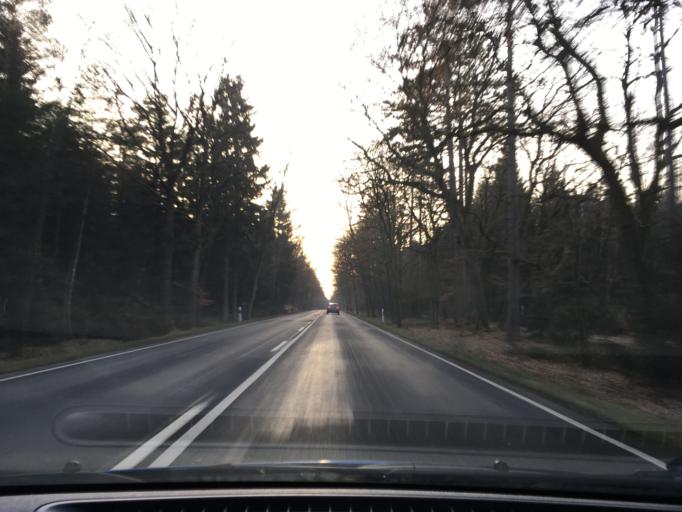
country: DE
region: Lower Saxony
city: Scharnhorst
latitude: 52.7607
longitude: 10.2893
